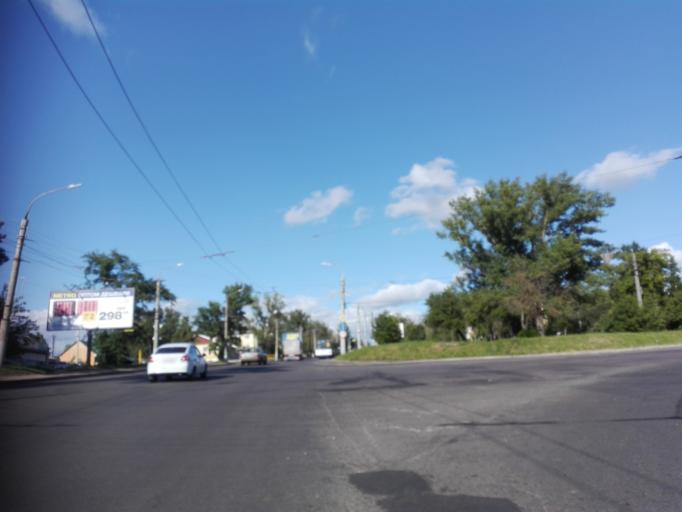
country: RU
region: Orjol
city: Orel
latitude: 52.9849
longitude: 36.1104
